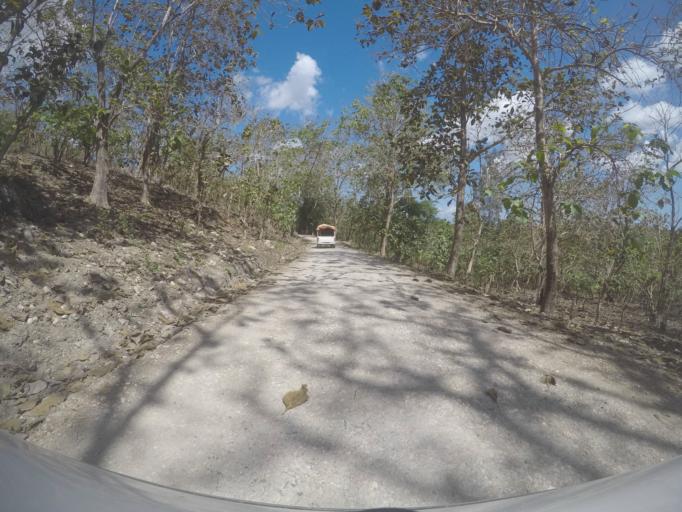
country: TL
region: Viqueque
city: Viqueque
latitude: -8.8956
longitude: 126.3887
